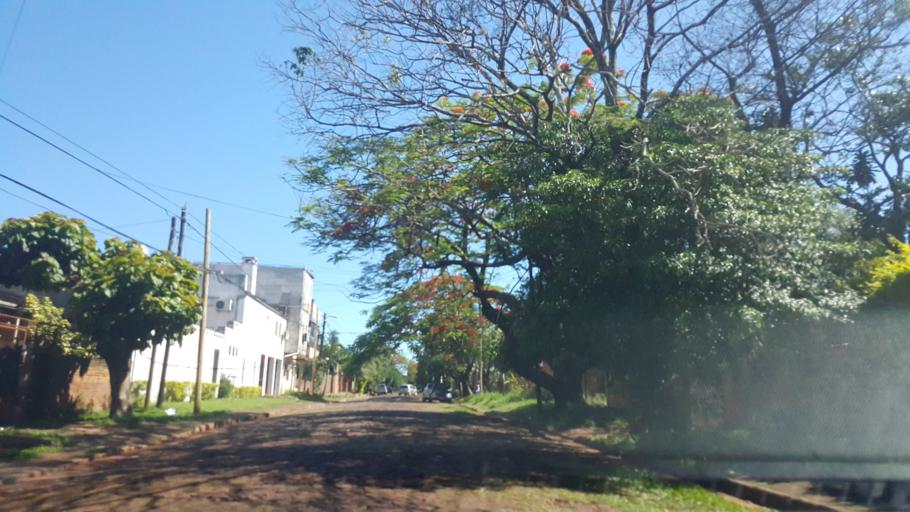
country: AR
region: Misiones
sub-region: Departamento de Capital
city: Posadas
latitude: -27.3897
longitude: -55.9056
